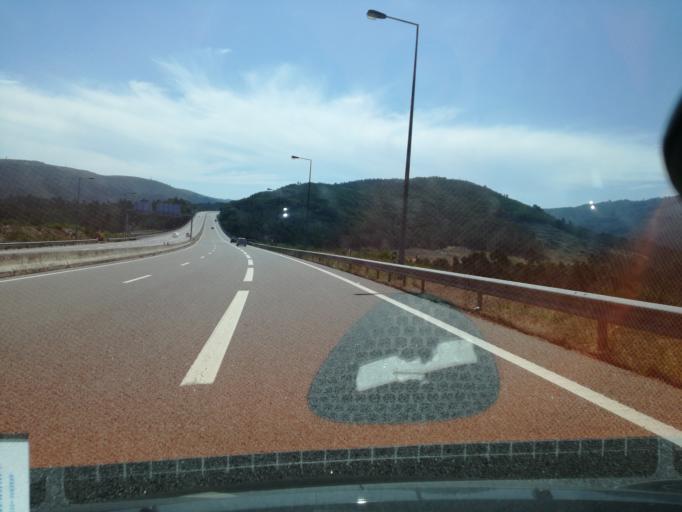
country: PT
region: Viana do Castelo
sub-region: Caminha
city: Vila Praia de Ancora
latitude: 41.8022
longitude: -8.8014
